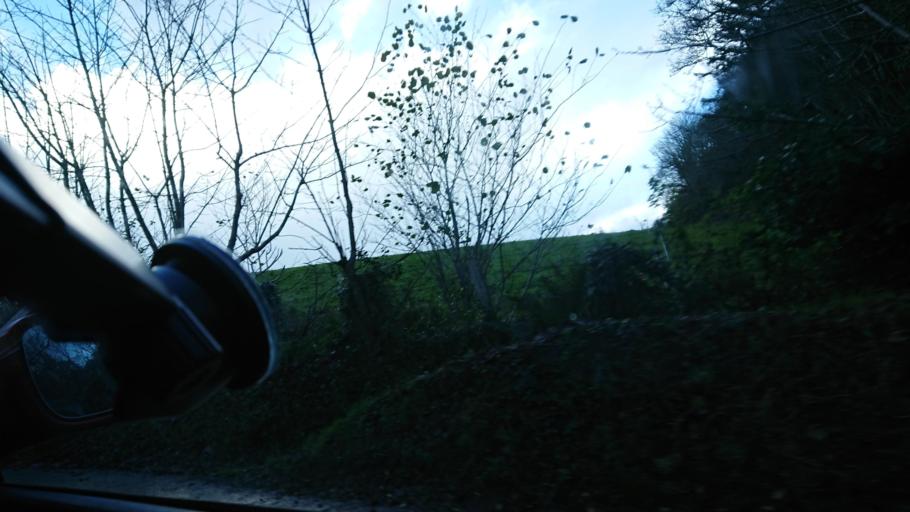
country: GB
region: England
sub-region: Cornwall
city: Looe
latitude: 50.3433
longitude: -4.4800
